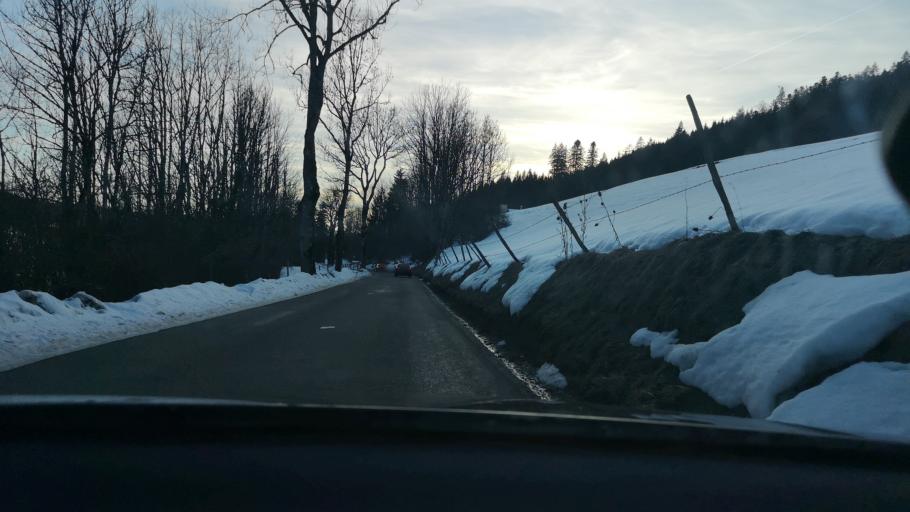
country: FR
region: Franche-Comte
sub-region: Departement du Doubs
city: La Cluse-et-Mijoux
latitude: 46.9205
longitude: 6.3921
